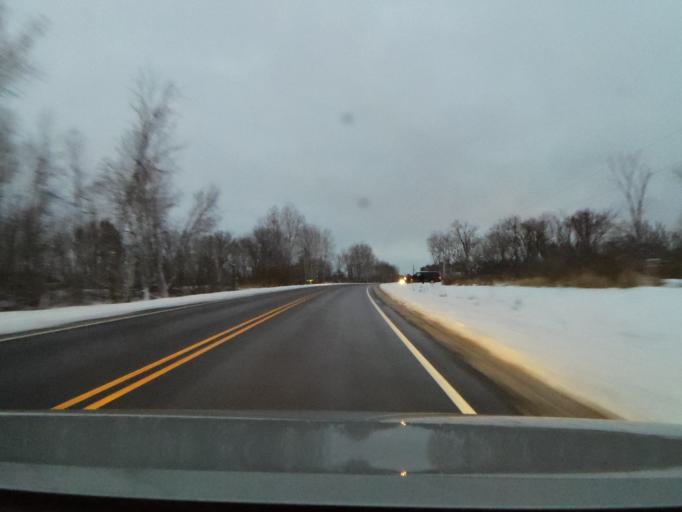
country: US
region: Wisconsin
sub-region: Dunn County
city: Menomonie
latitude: 44.9276
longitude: -91.9848
